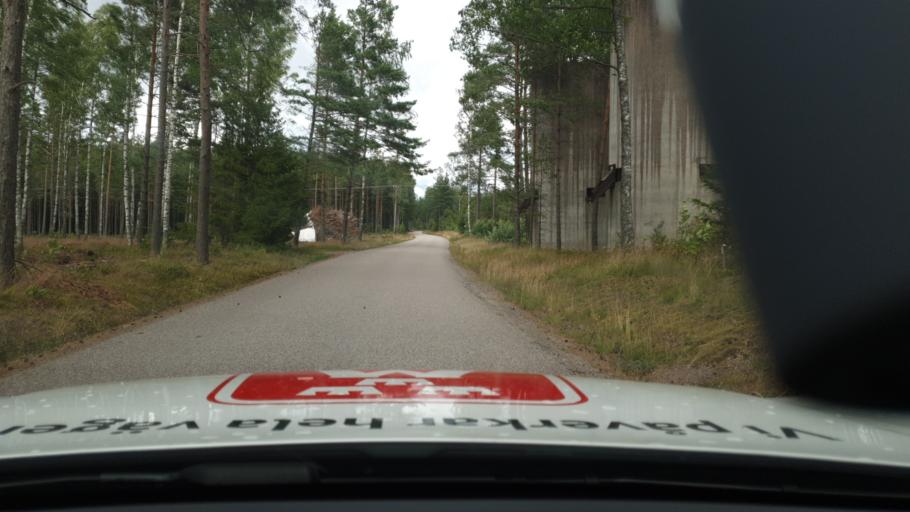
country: SE
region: Vaestra Goetaland
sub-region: Toreboda Kommun
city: Toereboda
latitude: 58.7108
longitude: 14.1762
